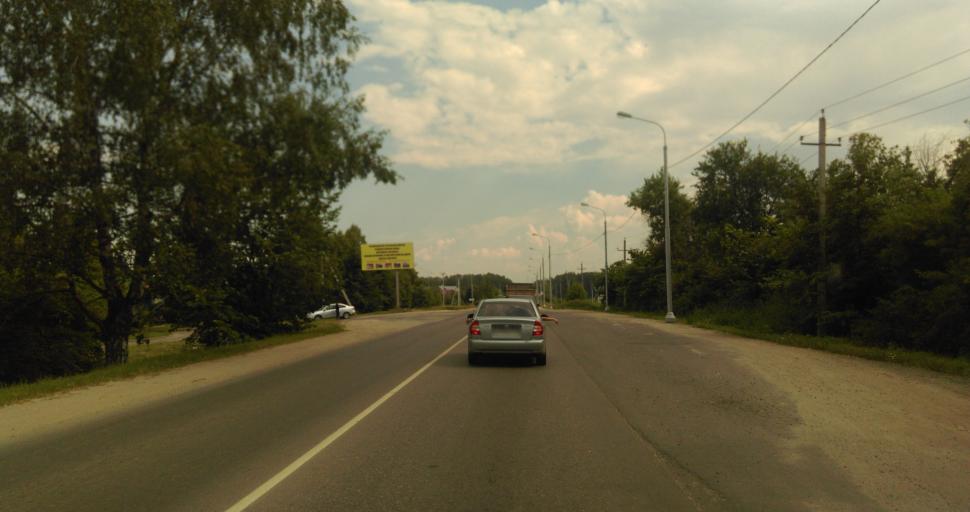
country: RU
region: Moskovskaya
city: Zhitnevo
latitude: 55.3417
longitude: 37.9058
